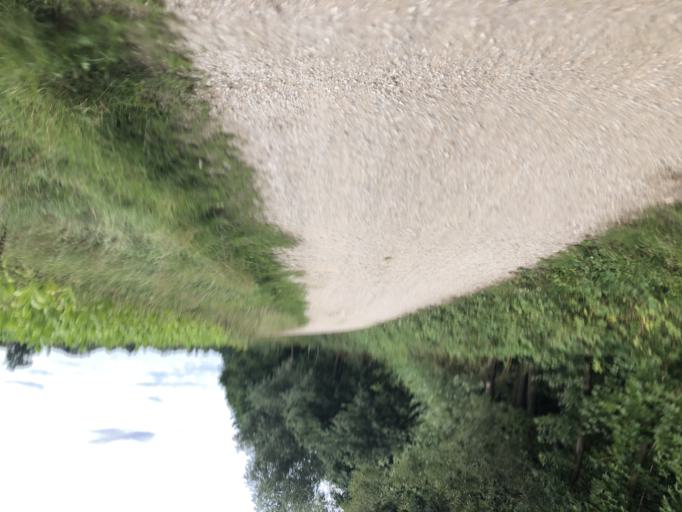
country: DE
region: Bavaria
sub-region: Regierungsbezirk Mittelfranken
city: Furth
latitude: 49.5305
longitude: 11.0016
